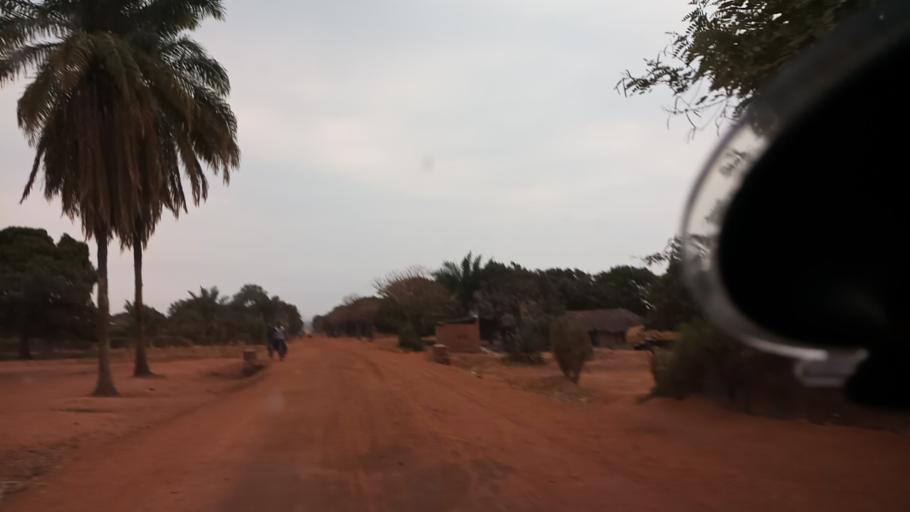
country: ZM
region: Luapula
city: Nchelenge
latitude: -9.2770
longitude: 28.3261
